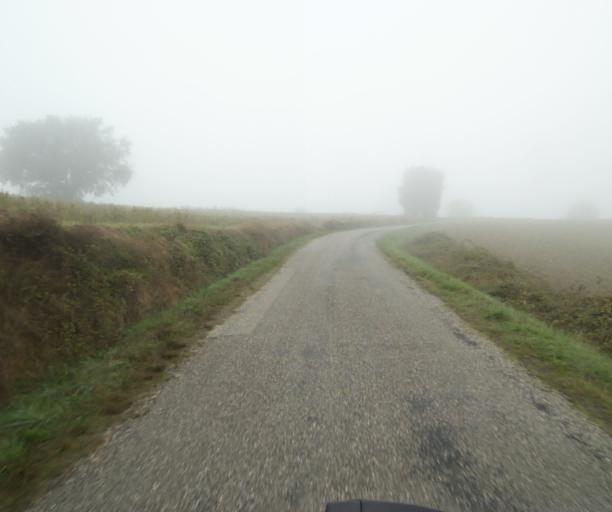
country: FR
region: Midi-Pyrenees
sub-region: Departement de la Haute-Garonne
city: Villemur-sur-Tarn
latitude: 43.8985
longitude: 1.4883
